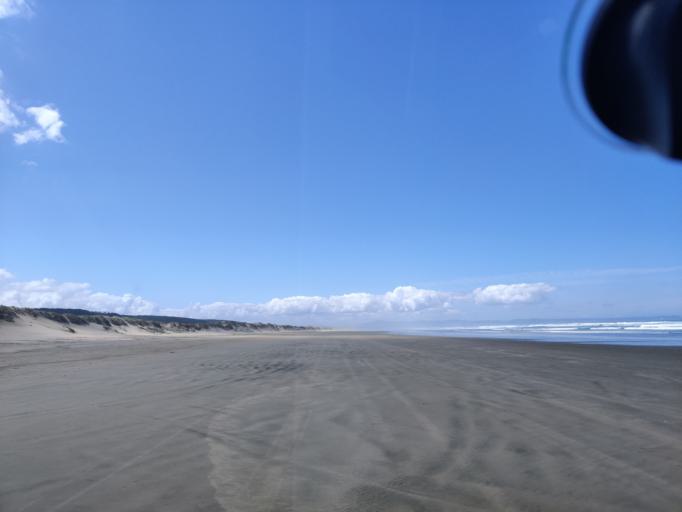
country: NZ
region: Northland
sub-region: Far North District
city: Kaitaia
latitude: -34.9486
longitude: 173.1205
